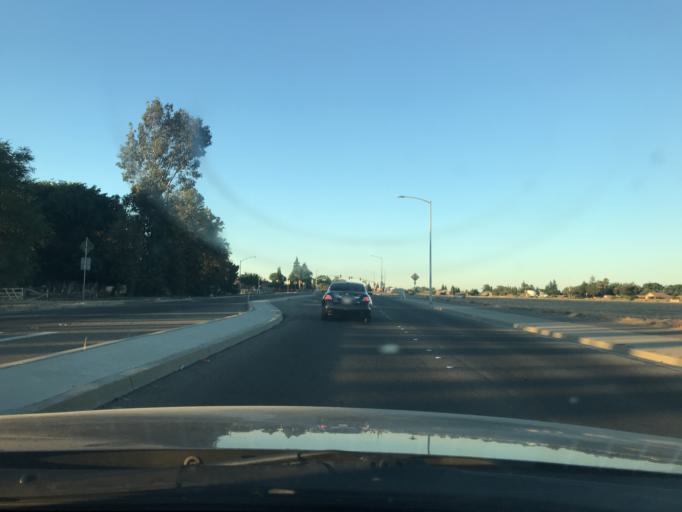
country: US
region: California
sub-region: Merced County
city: Atwater
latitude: 37.3520
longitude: -120.5768
